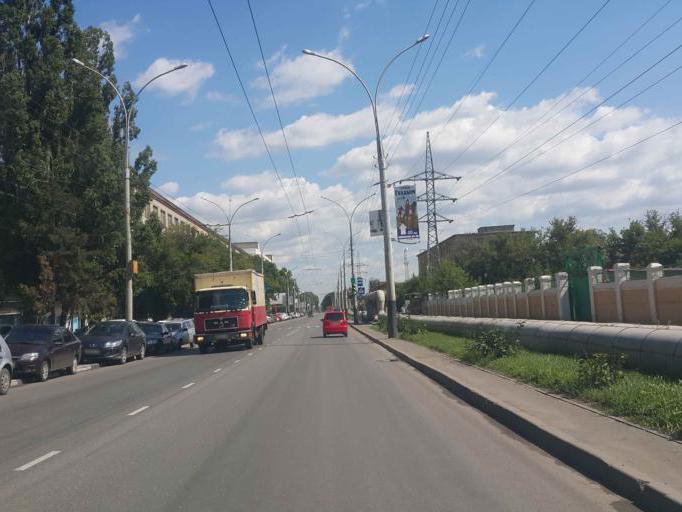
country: RU
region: Tambov
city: Tambov
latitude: 52.7492
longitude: 41.4609
